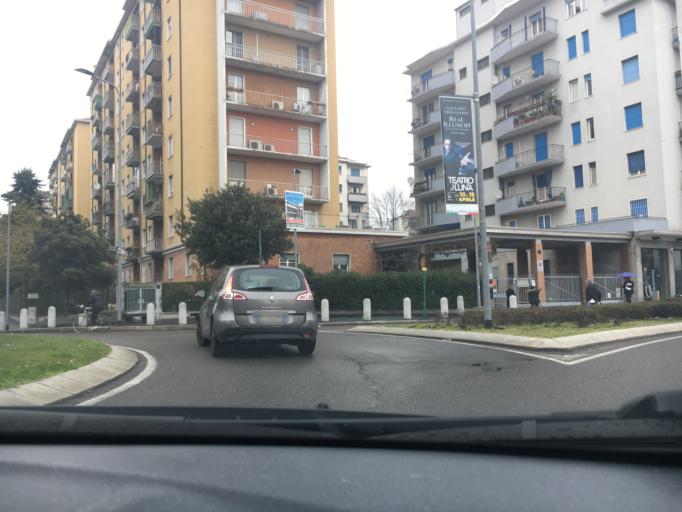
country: IT
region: Lombardy
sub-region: Citta metropolitana di Milano
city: Romano Banco
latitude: 45.4649
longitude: 9.1431
